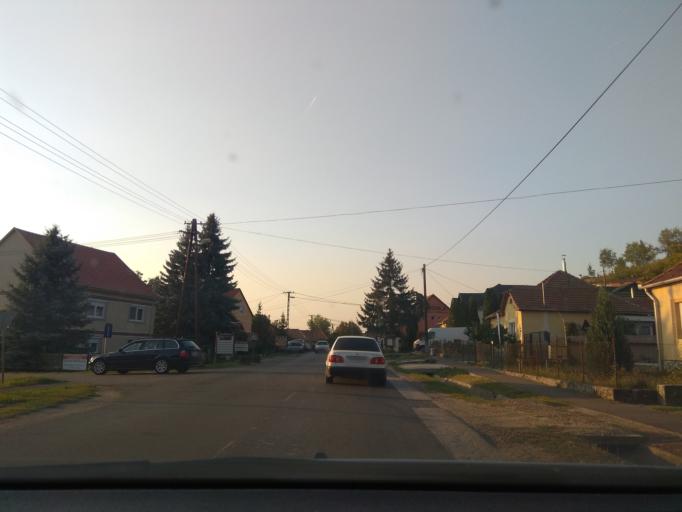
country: HU
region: Heves
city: Egerszalok
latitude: 47.8663
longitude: 20.3265
